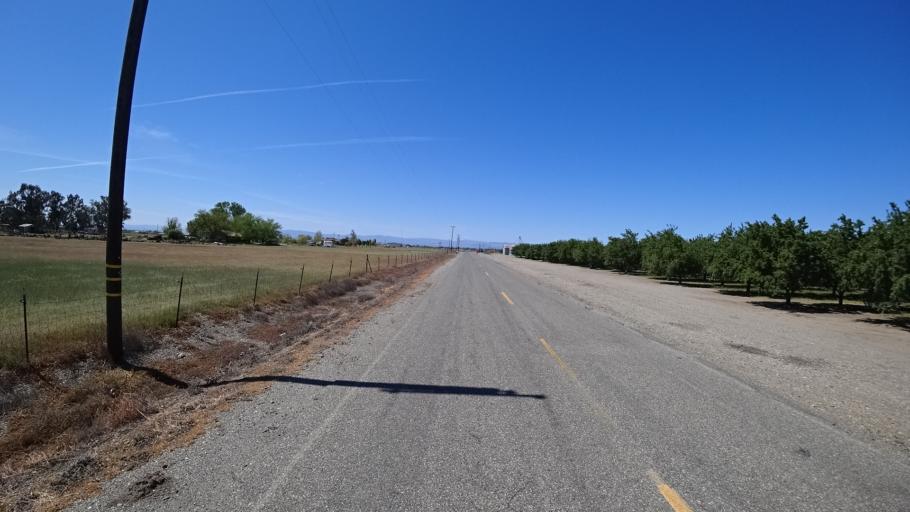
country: US
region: California
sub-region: Glenn County
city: Orland
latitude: 39.7251
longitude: -122.1375
